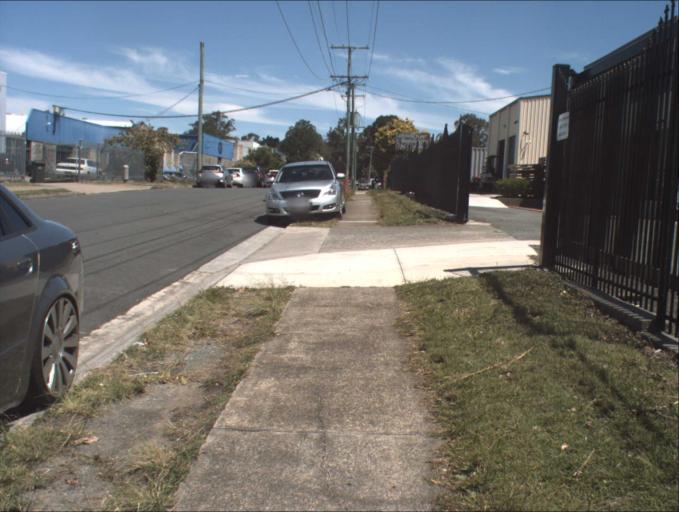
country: AU
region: Queensland
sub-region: Logan
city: Woodridge
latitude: -27.6194
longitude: 153.1082
